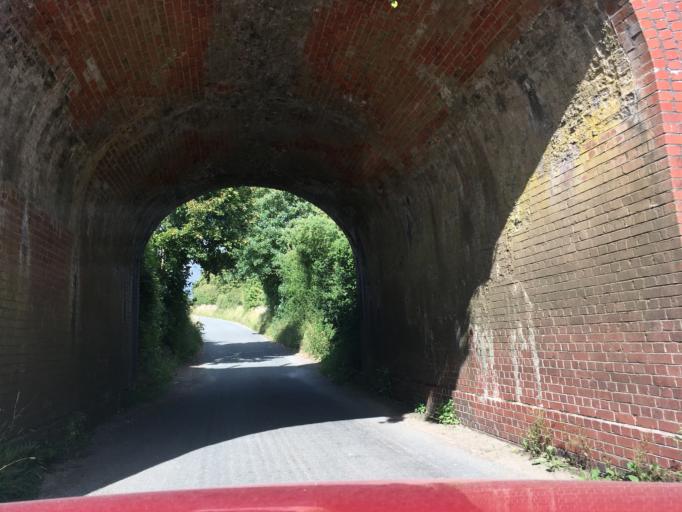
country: GB
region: England
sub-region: Gloucestershire
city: Coates
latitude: 51.7008
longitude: -2.0450
